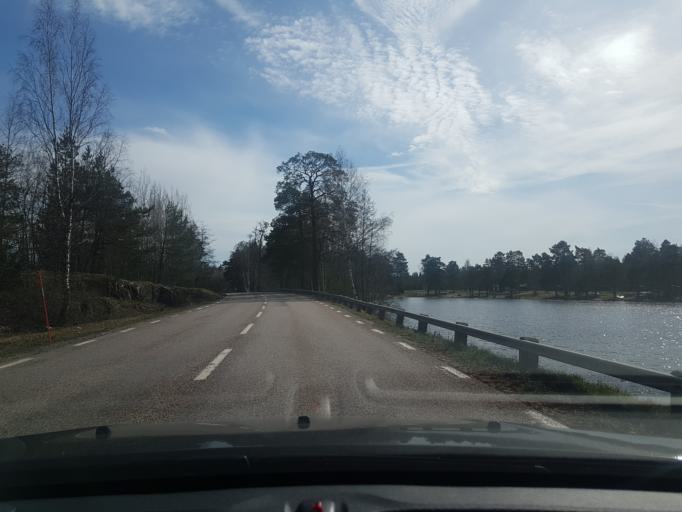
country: SE
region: Vaestmanland
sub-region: Sala Kommun
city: Sala
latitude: 59.9580
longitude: 16.5154
